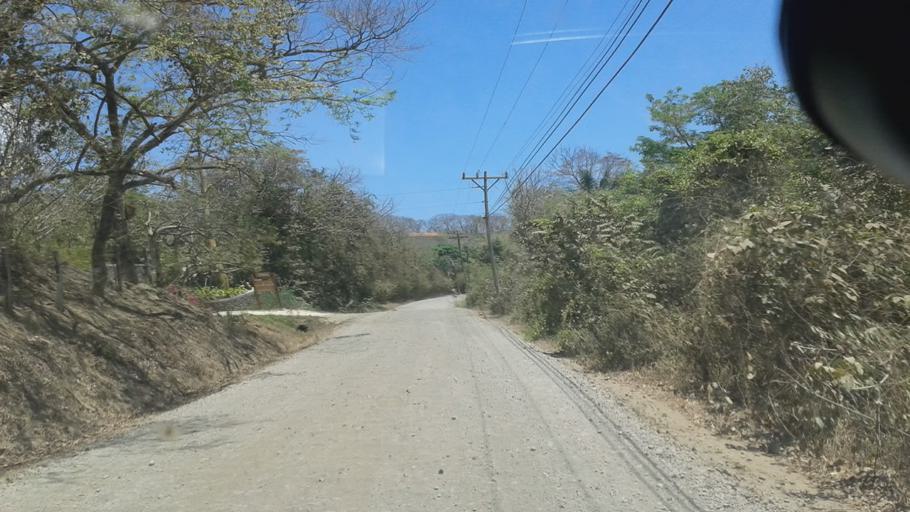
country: CR
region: Guanacaste
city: Samara
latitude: 10.0021
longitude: -85.7066
